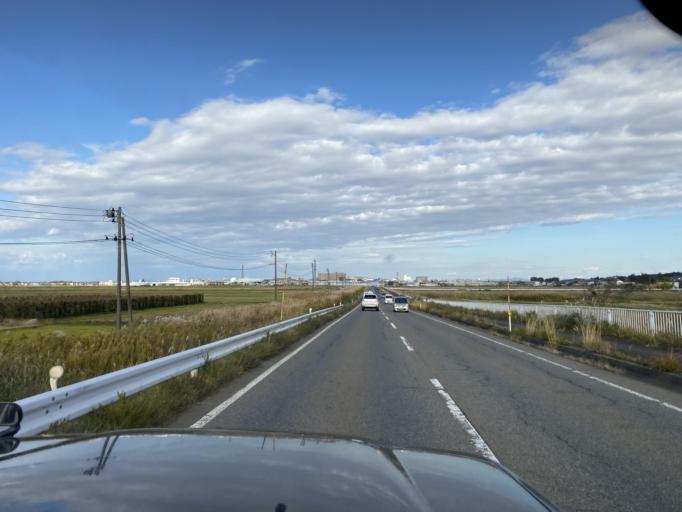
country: JP
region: Niigata
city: Niitsu-honcho
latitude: 37.7779
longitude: 139.1079
